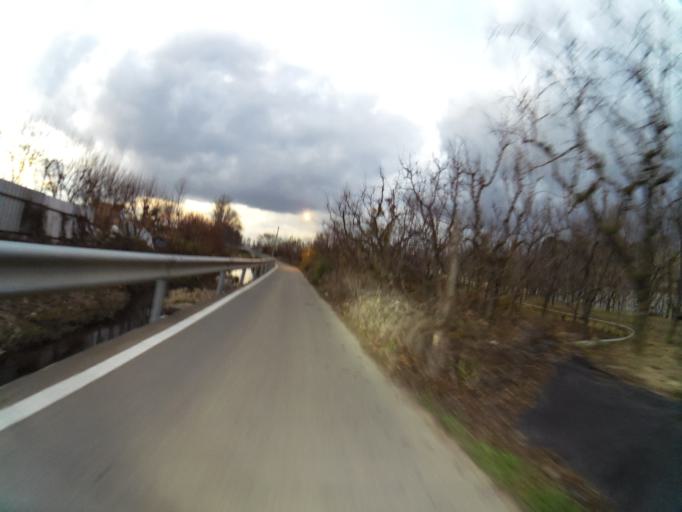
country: KR
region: Gyeongsangbuk-do
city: Gyeongsan-si
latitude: 35.8389
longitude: 128.7491
